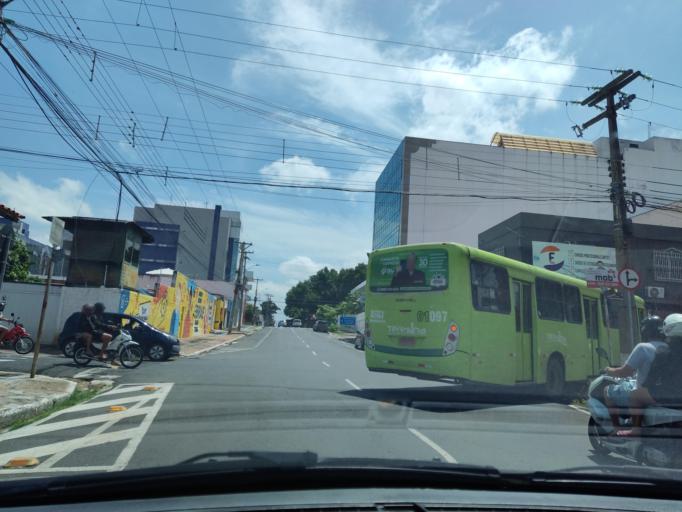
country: BR
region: Piaui
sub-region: Teresina
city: Teresina
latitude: -5.0859
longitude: -42.8190
